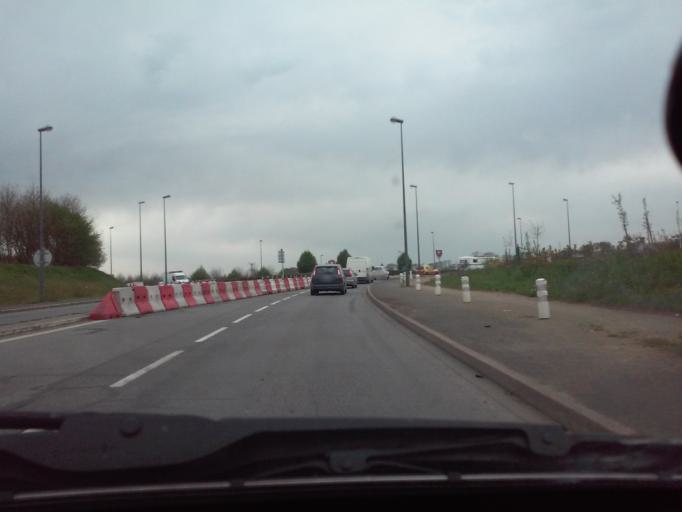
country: FR
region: Brittany
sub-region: Departement d'Ille-et-Vilaine
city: Lecousse
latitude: 48.3516
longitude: -1.2330
